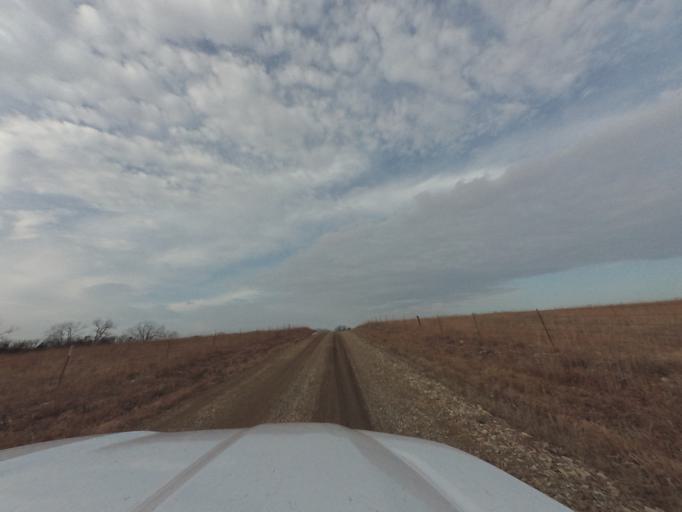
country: US
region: Kansas
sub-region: Chase County
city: Cottonwood Falls
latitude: 38.4785
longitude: -96.4156
